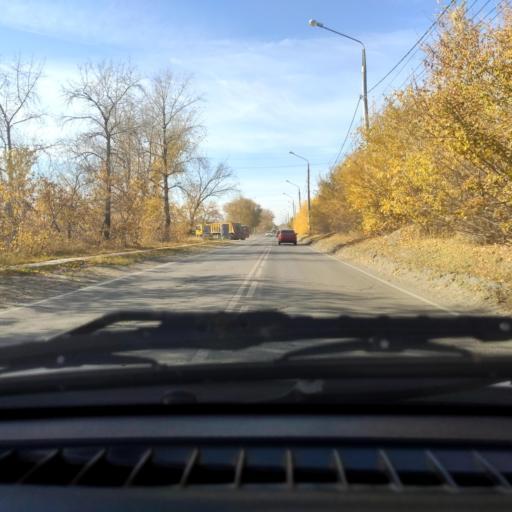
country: RU
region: Samara
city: Zhigulevsk
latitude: 53.4636
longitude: 49.5583
